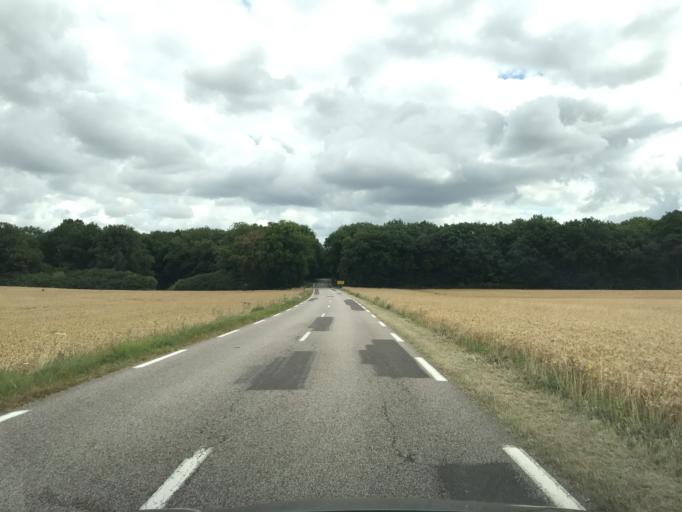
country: FR
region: Haute-Normandie
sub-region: Departement de l'Eure
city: Menilles
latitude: 49.0386
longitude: 1.3008
